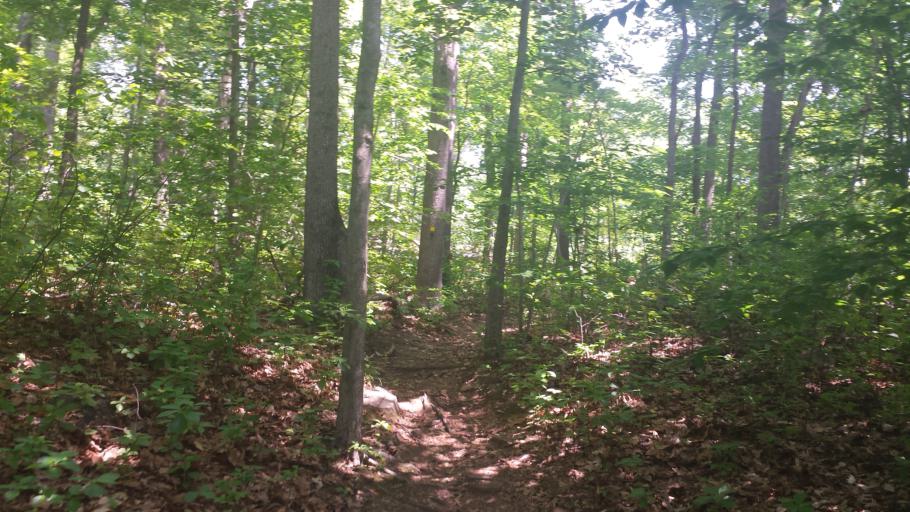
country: US
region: New York
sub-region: Westchester County
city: Valhalla
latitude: 41.0751
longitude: -73.7564
